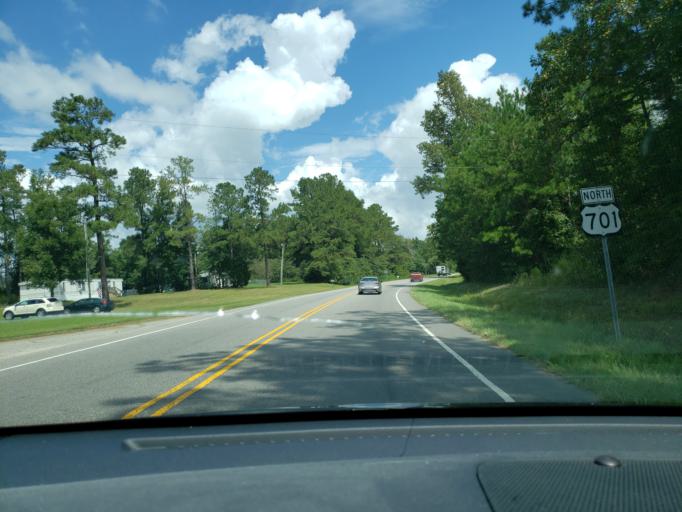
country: US
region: North Carolina
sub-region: Columbus County
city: Brunswick
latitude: 34.2491
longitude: -78.7541
